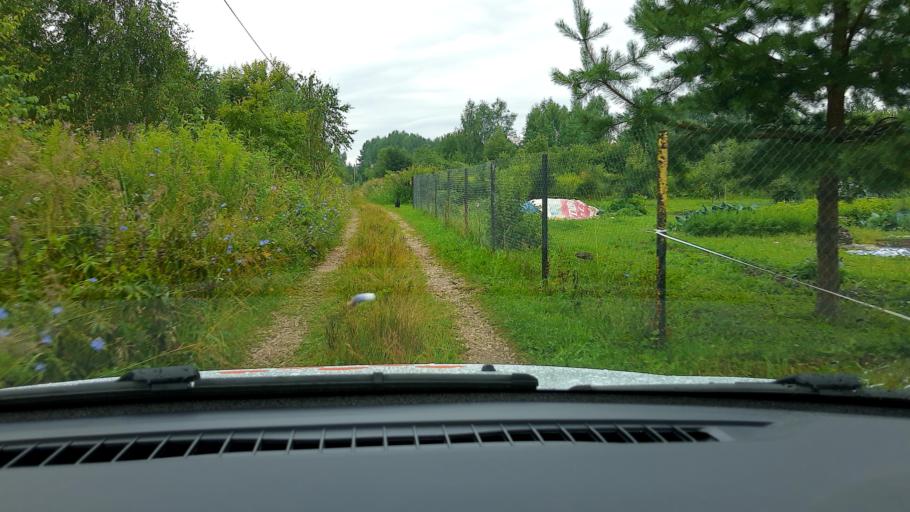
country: RU
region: Nizjnij Novgorod
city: Surovatikha
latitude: 55.9312
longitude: 43.9271
